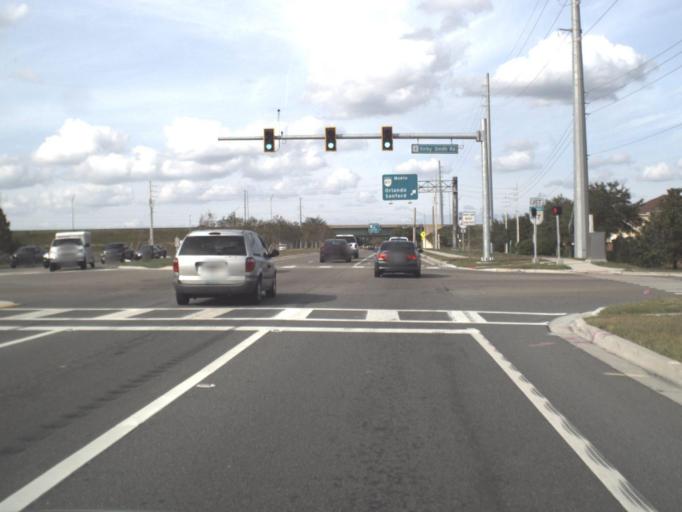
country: US
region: Florida
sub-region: Orange County
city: Meadow Woods
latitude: 28.3973
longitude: -81.2443
